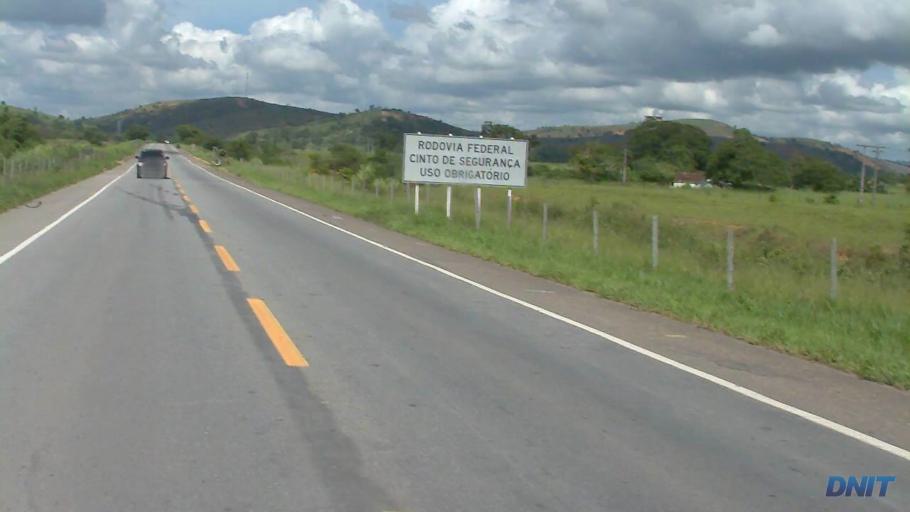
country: BR
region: Minas Gerais
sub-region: Governador Valadares
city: Governador Valadares
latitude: -19.0083
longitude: -42.1347
